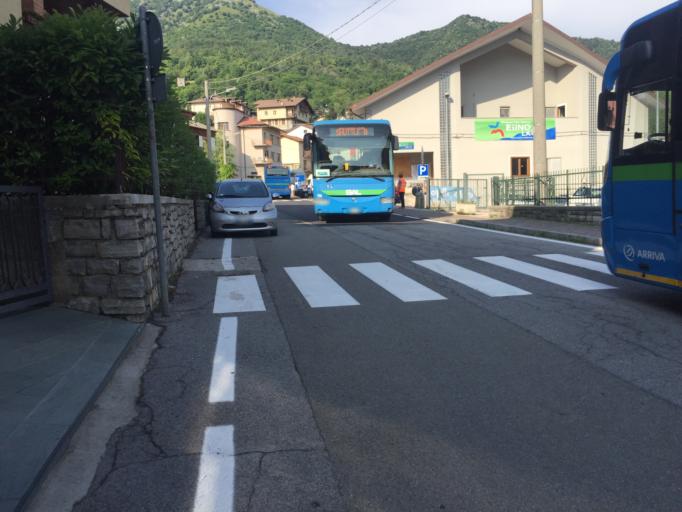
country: IT
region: Lombardy
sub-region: Provincia di Lecco
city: Esino Lario
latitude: 45.9930
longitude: 9.3298
